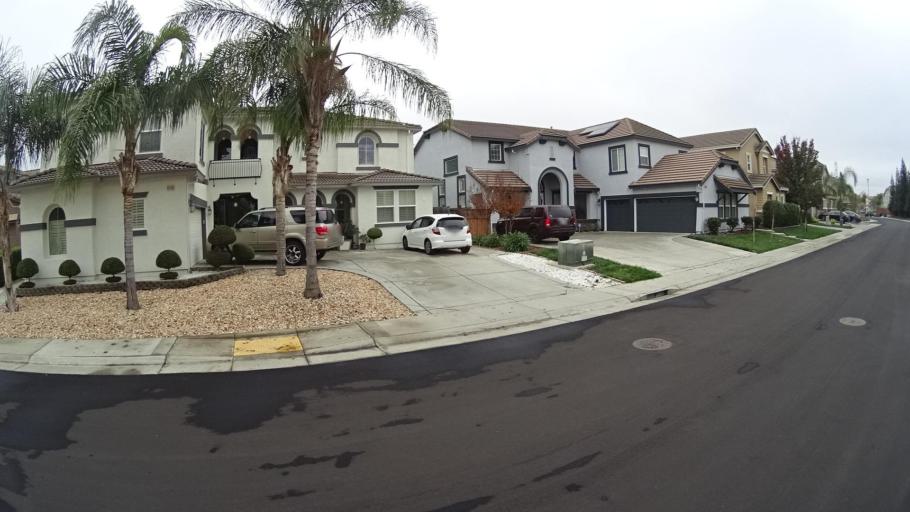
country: US
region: California
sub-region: Sacramento County
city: Elk Grove
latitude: 38.3954
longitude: -121.3461
